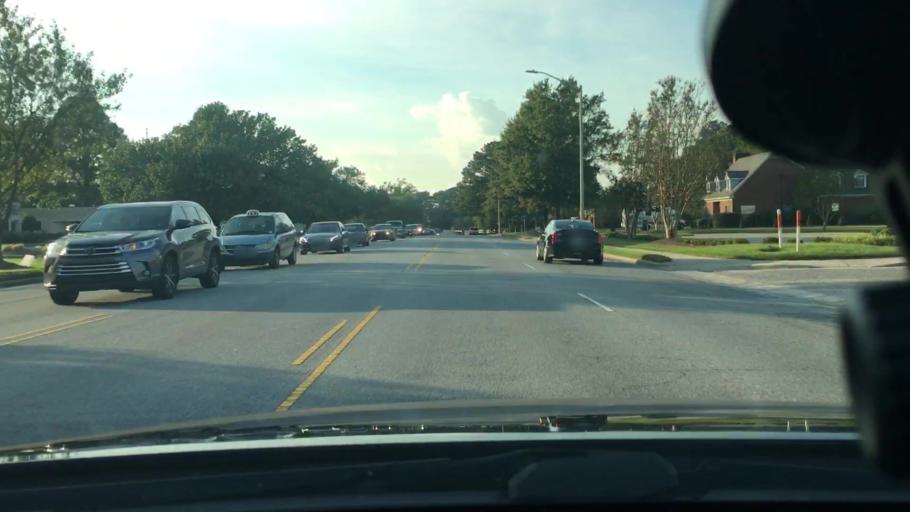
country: US
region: North Carolina
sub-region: Pitt County
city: Greenville
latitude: 35.5889
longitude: -77.3750
